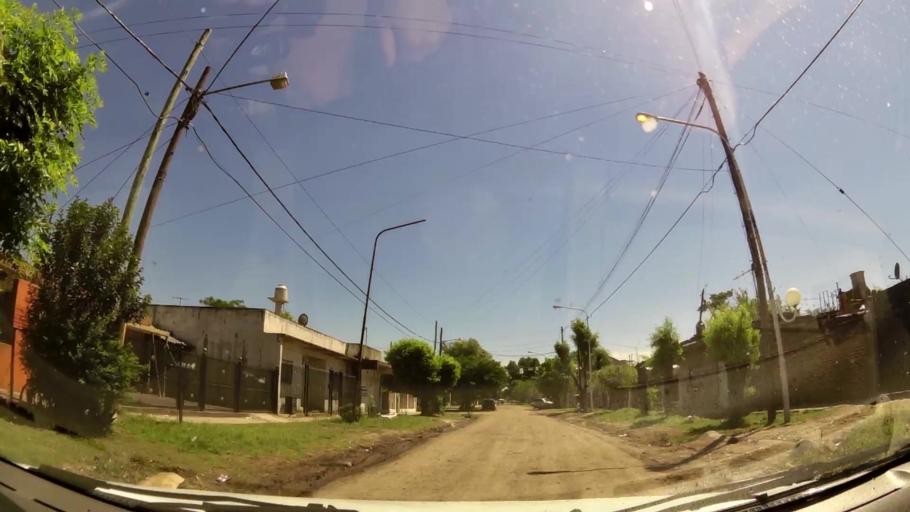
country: AR
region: Buenos Aires
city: Ituzaingo
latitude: -34.6849
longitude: -58.6672
